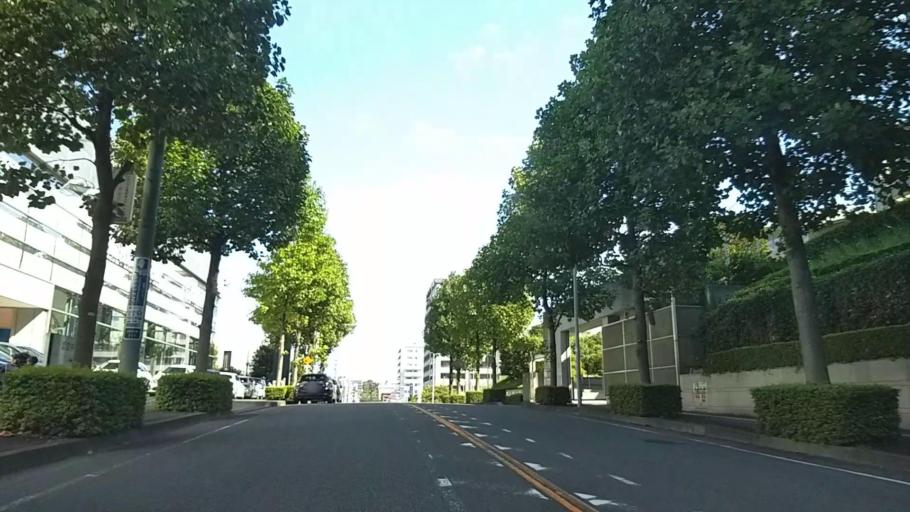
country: JP
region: Tokyo
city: Chofugaoka
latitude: 35.5658
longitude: 139.5537
